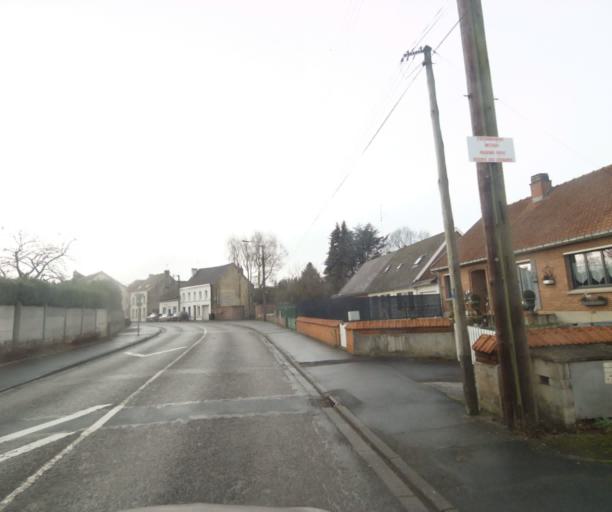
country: FR
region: Nord-Pas-de-Calais
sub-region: Departement du Nord
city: Famars
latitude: 50.3134
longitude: 3.5182
